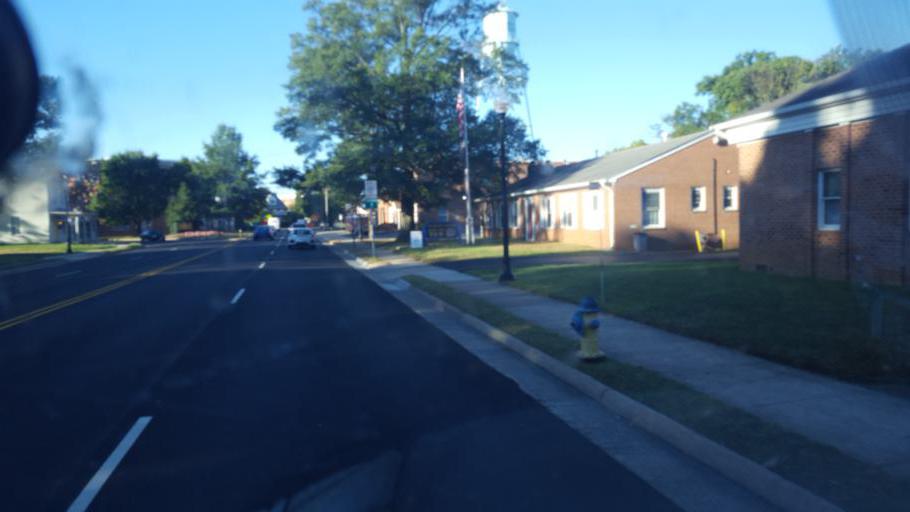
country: US
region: Virginia
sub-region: City of Manassas
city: Manassas
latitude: 38.7535
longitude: -77.4681
